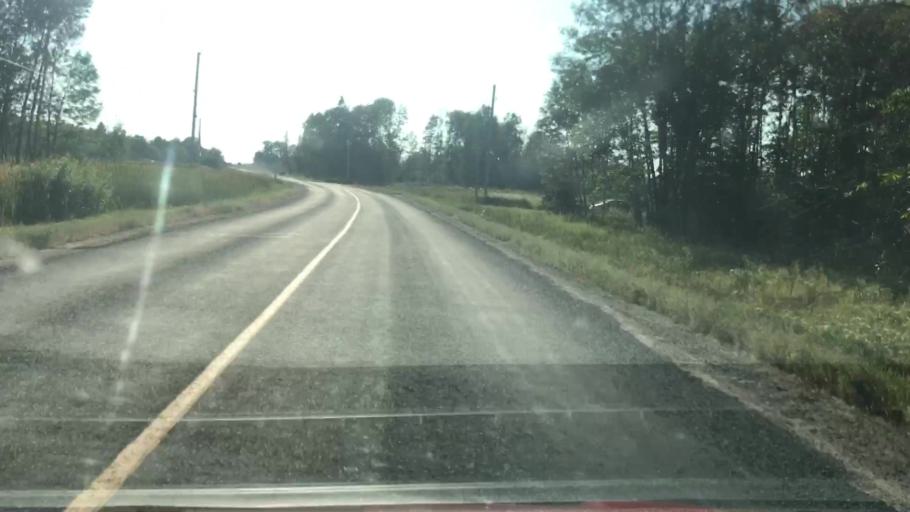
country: US
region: Michigan
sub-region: Chippewa County
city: Sault Ste. Marie
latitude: 46.2871
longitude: -84.0513
